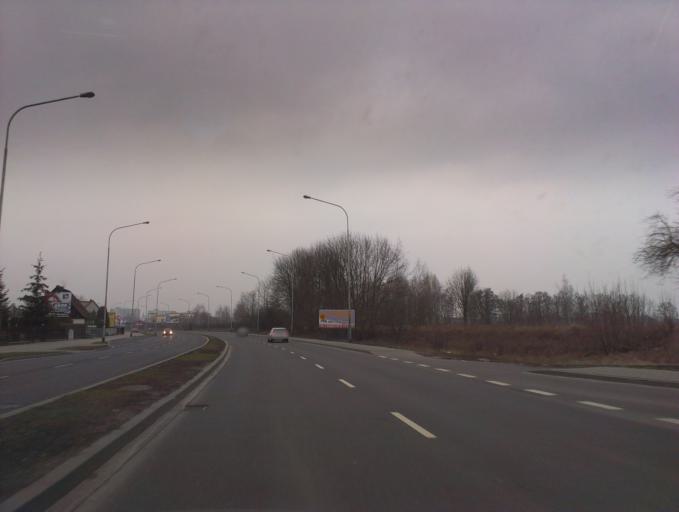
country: PL
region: Greater Poland Voivodeship
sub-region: Powiat pilski
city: Pila
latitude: 53.1401
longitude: 16.7501
